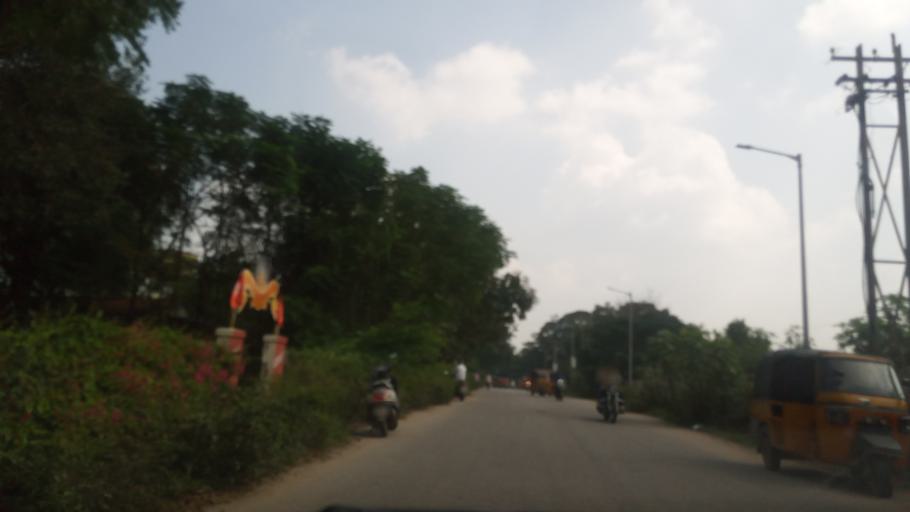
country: IN
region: Tamil Nadu
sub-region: Vellore
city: Arakkonam
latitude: 13.0822
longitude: 79.6666
